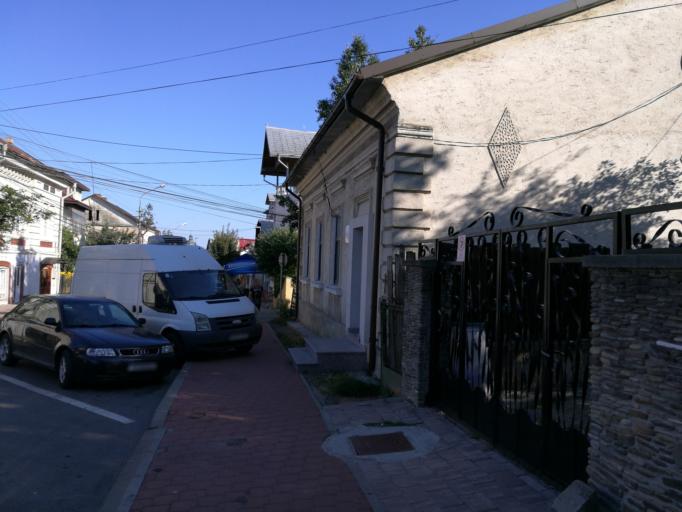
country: RO
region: Suceava
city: Suceava
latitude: 47.6493
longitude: 26.2566
